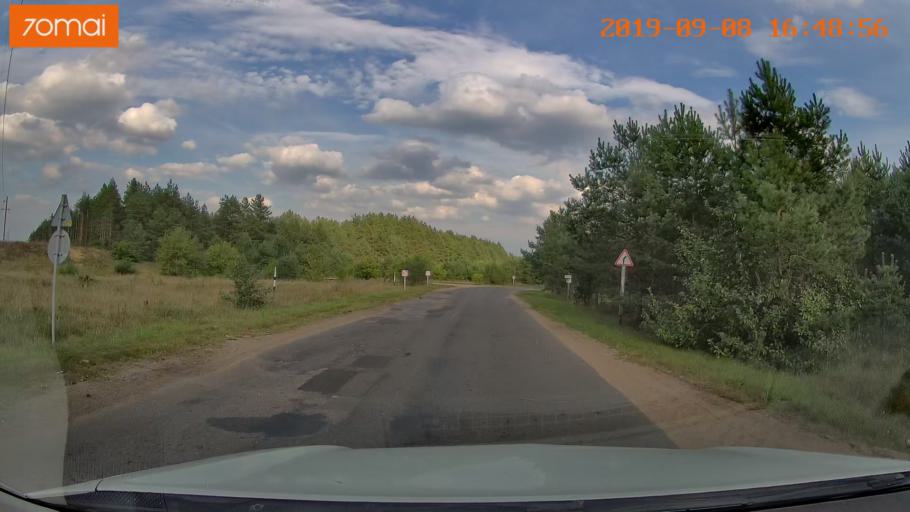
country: BY
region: Grodnenskaya
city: Hrodna
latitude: 53.8111
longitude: 23.8652
